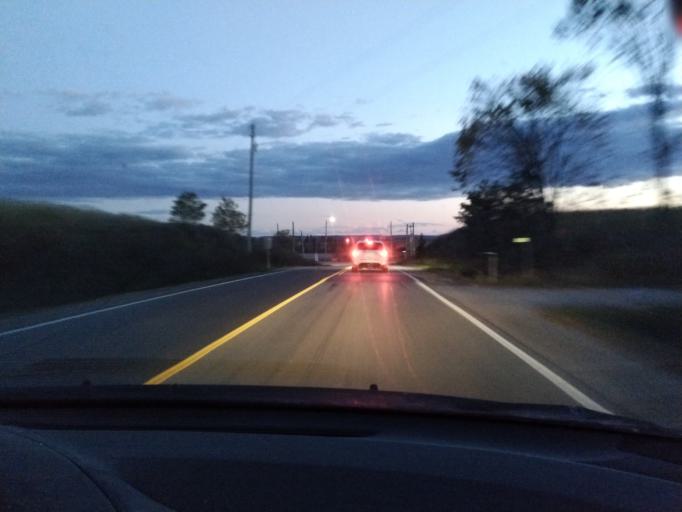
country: CA
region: Ontario
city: Bradford West Gwillimbury
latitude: 44.0990
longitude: -79.6391
